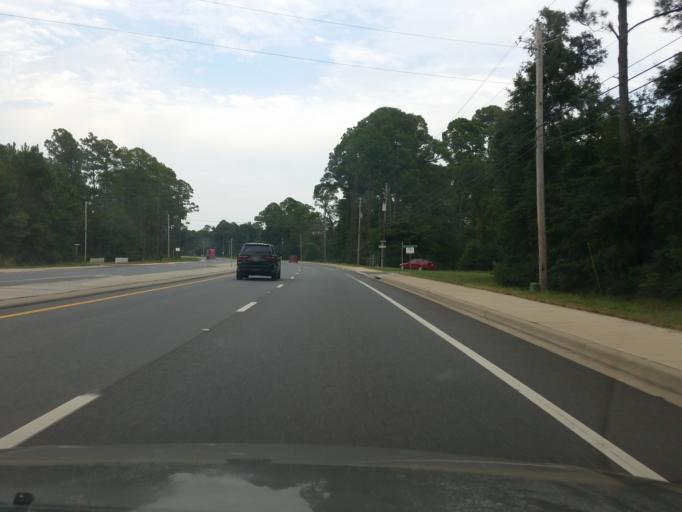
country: US
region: Florida
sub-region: Santa Rosa County
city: Holley
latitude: 30.4479
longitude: -86.9017
